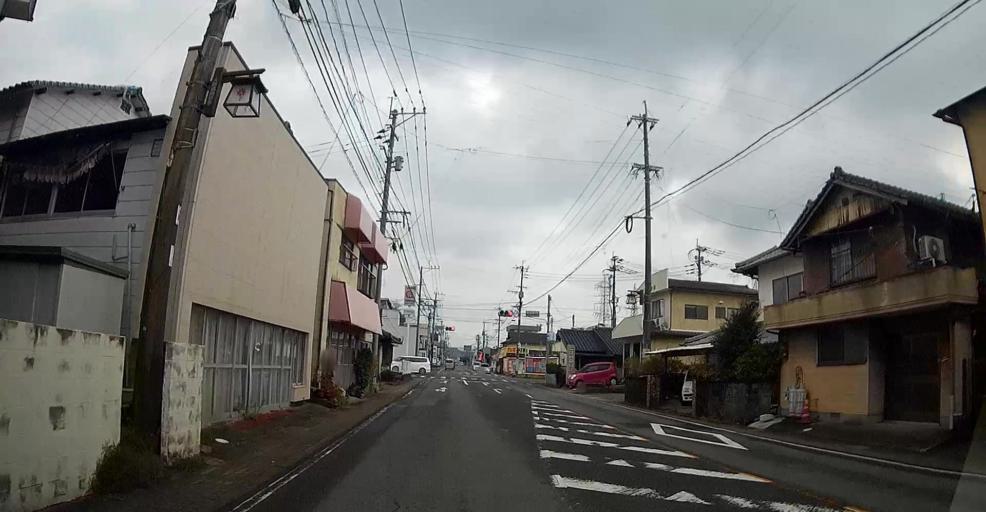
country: JP
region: Kumamoto
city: Matsubase
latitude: 32.6510
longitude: 130.6880
